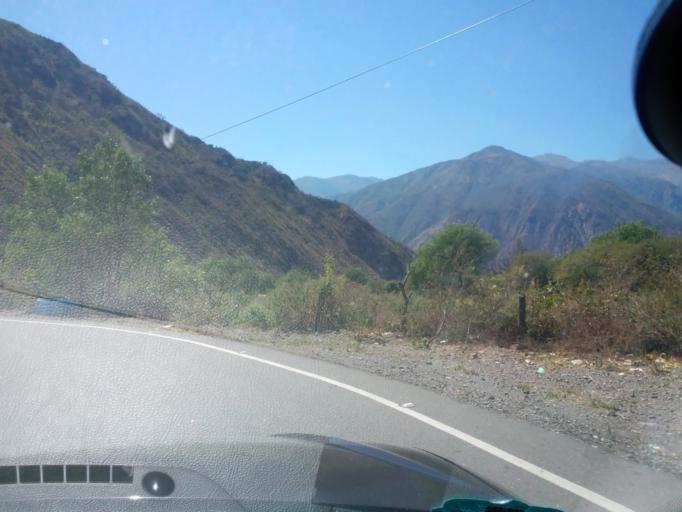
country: PE
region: Ayacucho
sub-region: Provincia de Huamanga
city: Ocros
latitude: -13.4242
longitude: -73.8640
